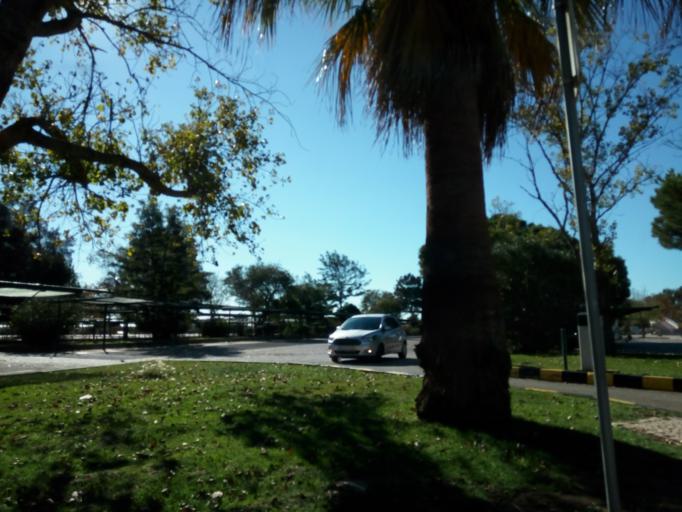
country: PT
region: Faro
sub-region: Loule
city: Vilamoura
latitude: 37.0775
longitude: -8.1284
